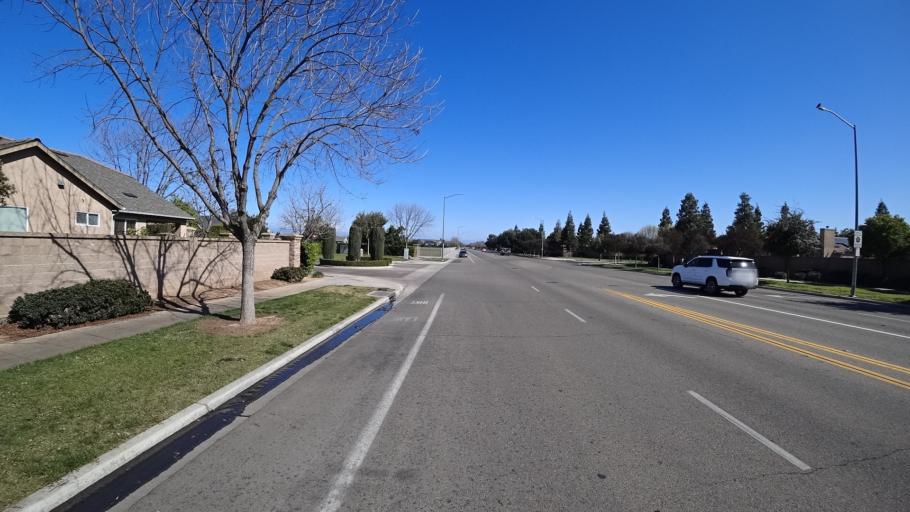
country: US
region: California
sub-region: Fresno County
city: Clovis
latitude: 36.8596
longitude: -119.7280
